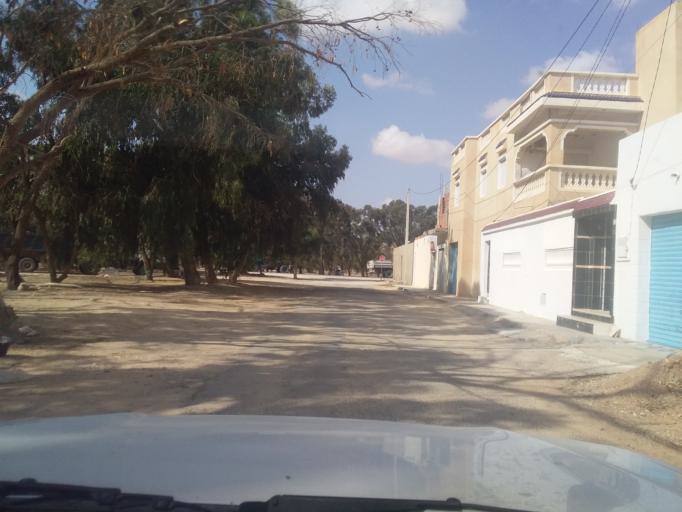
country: TN
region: Qabis
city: Gabes
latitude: 33.6229
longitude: 10.2796
